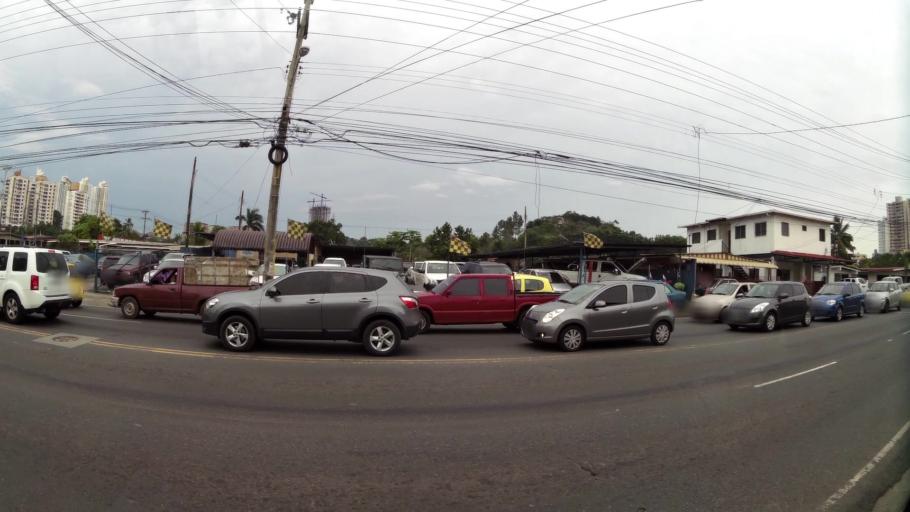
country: PA
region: Panama
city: Panama
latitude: 9.0198
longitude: -79.5230
